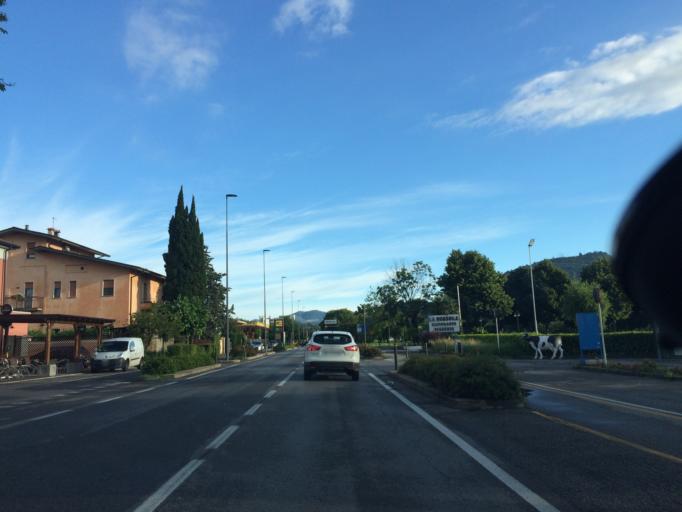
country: IT
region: Lombardy
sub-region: Provincia di Brescia
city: Brescia
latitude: 45.5208
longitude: 10.2464
